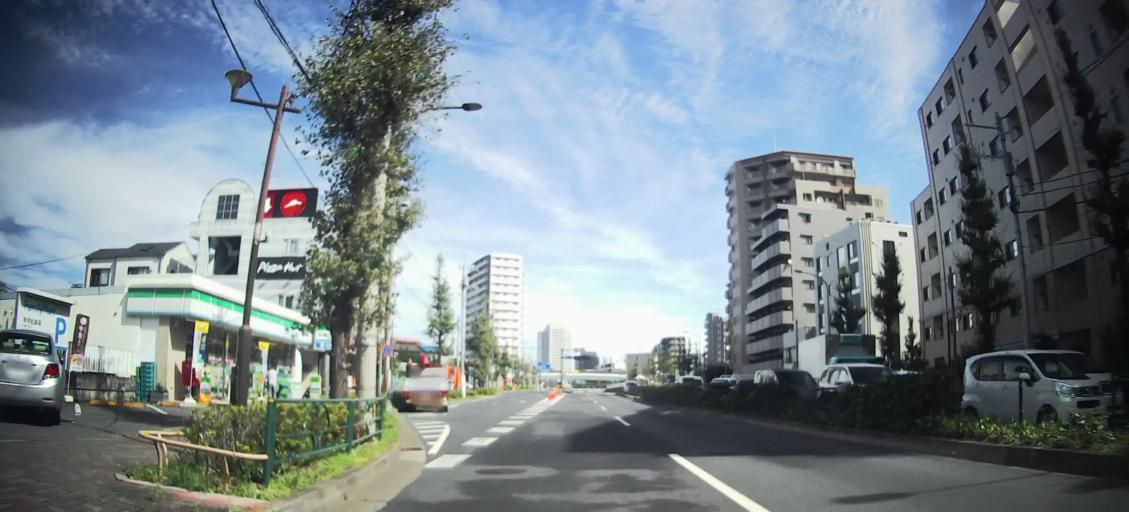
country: JP
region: Saitama
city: Wako
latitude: 35.7460
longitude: 139.6171
